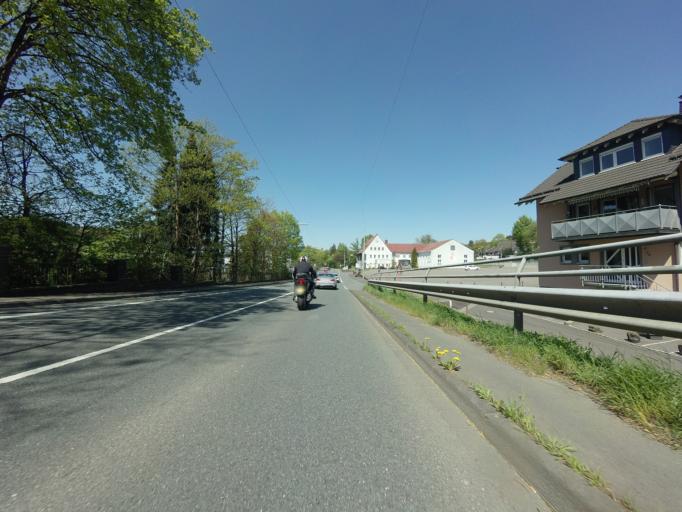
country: DE
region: North Rhine-Westphalia
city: Kreuztal
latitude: 50.9728
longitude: 7.9780
